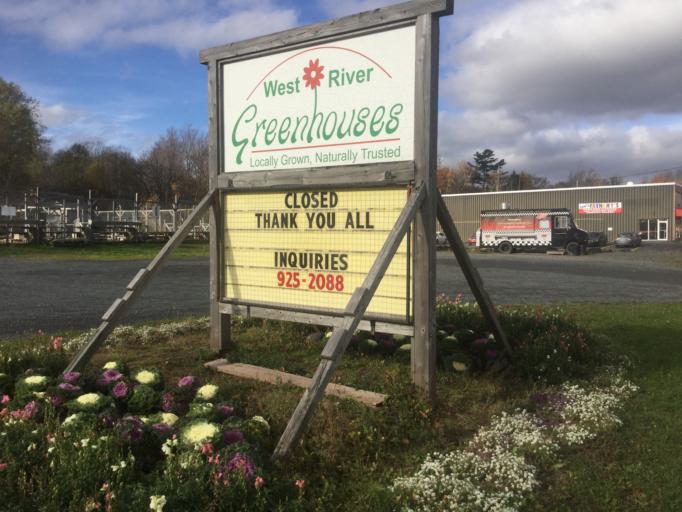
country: CA
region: Nova Scotia
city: New Glasgow
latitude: 45.5784
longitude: -62.6560
